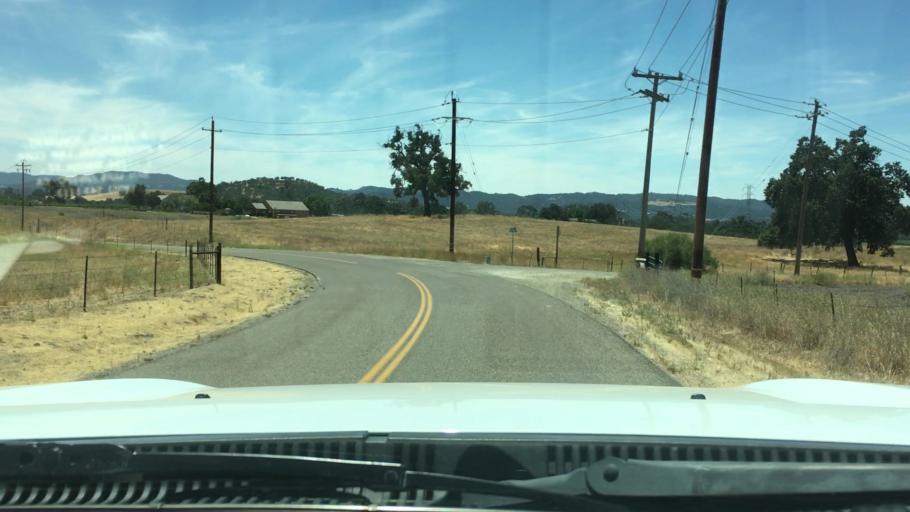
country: US
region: California
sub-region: San Luis Obispo County
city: Templeton
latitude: 35.5661
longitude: -120.6680
